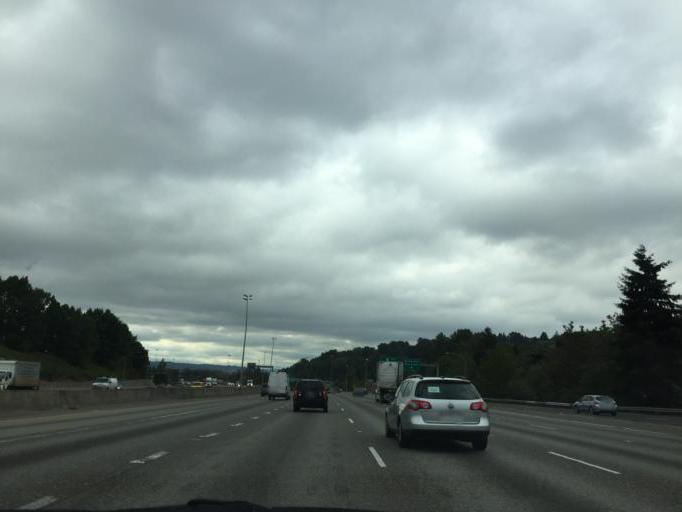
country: US
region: Washington
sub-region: King County
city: Tukwila
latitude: 47.4692
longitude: -122.2683
